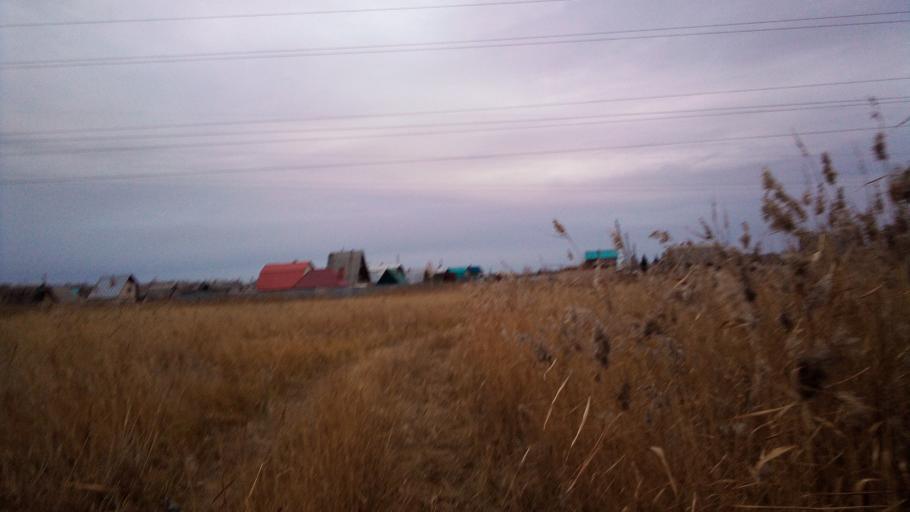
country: RU
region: Chelyabinsk
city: Novosineglazovskiy
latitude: 54.9858
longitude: 61.4033
